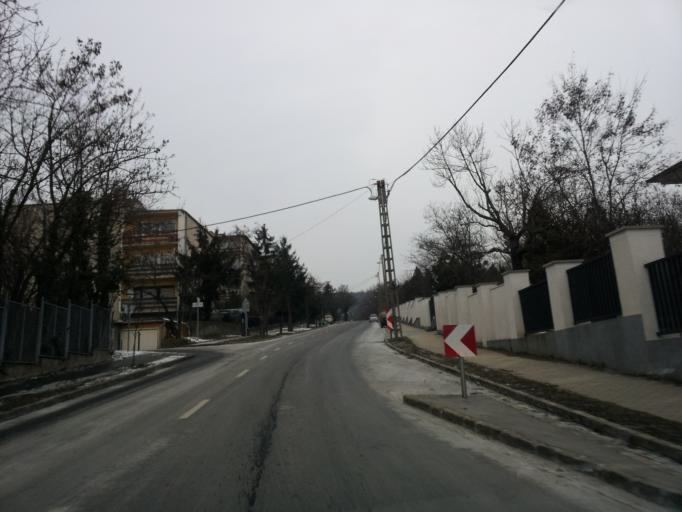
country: HU
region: Budapest
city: Budapest XII. keruelet
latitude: 47.4837
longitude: 18.9958
